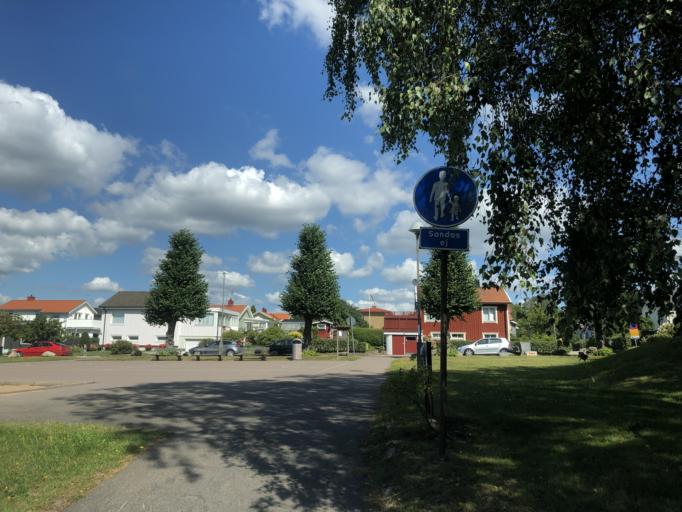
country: SE
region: Vaestra Goetaland
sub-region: Goteborg
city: Majorna
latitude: 57.7030
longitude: 11.9044
